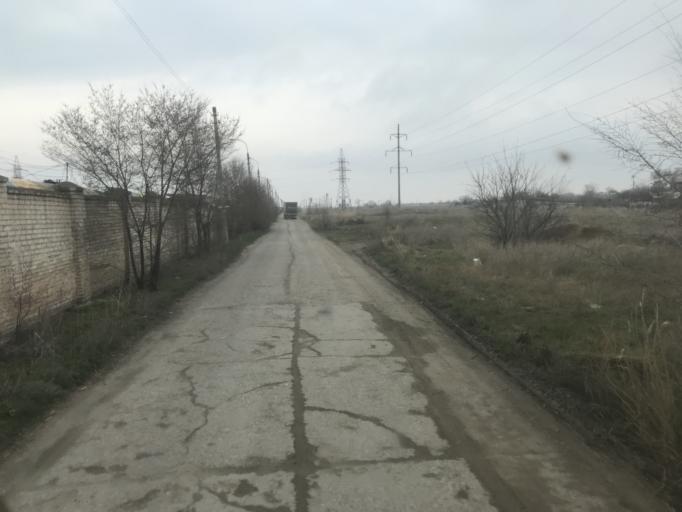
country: RU
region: Volgograd
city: Krasnoslobodsk
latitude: 48.5311
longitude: 44.5877
